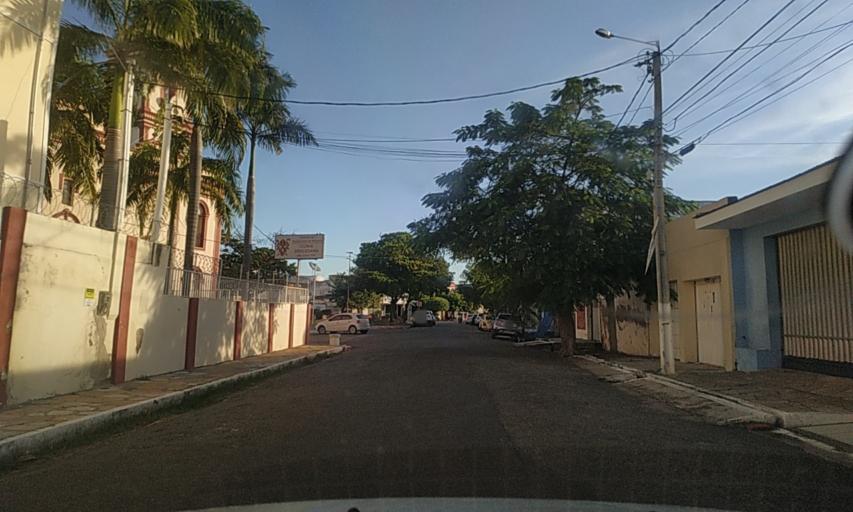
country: BR
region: Rio Grande do Norte
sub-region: Mossoro
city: Mossoro
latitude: -5.1931
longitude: -37.3401
